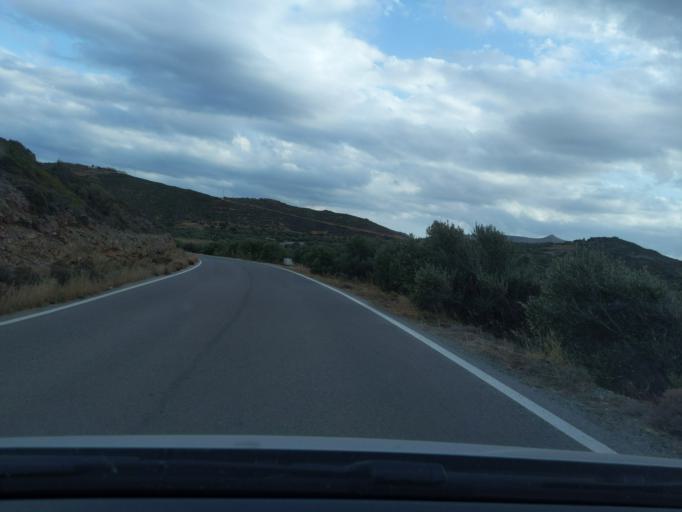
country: GR
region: Crete
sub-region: Nomos Lasithiou
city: Palekastro
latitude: 35.2250
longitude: 26.2568
